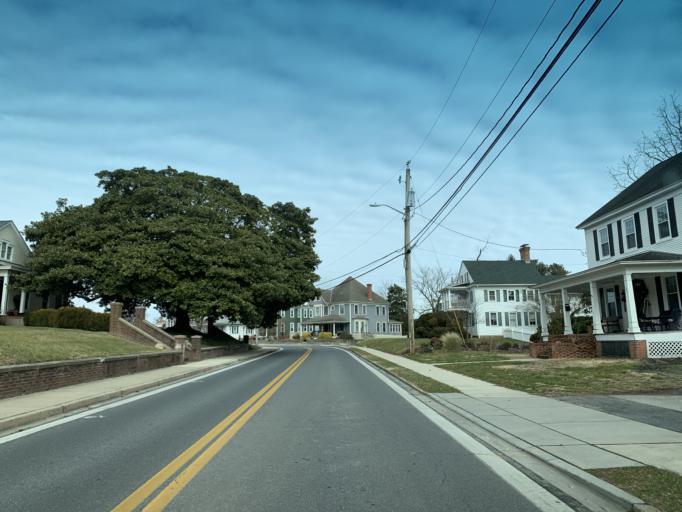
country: US
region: Maryland
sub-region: Worcester County
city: Berlin
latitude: 38.3220
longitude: -75.2184
